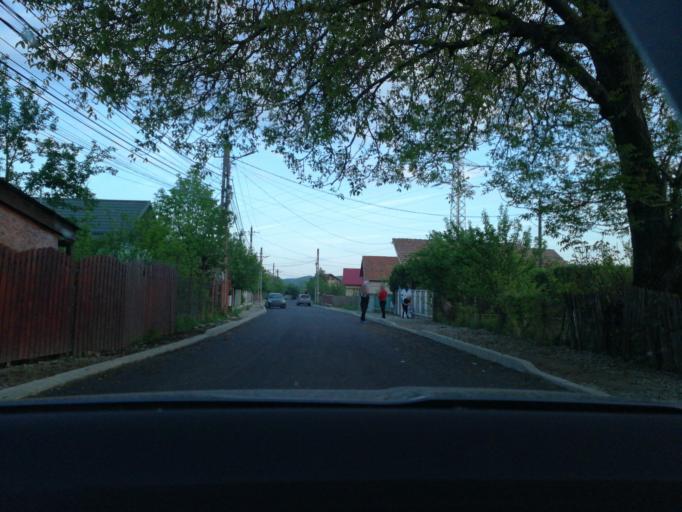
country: RO
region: Prahova
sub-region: Comuna Cornu
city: Cornu de Jos
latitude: 45.1474
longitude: 25.7020
